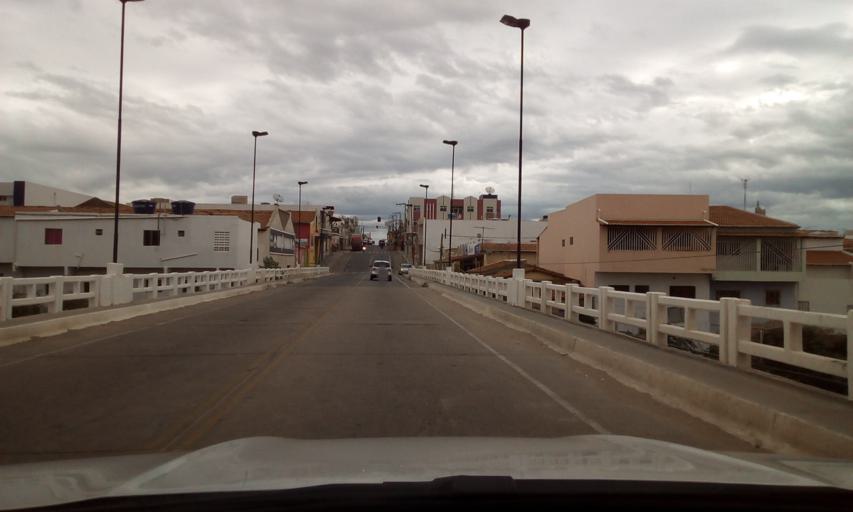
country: BR
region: Paraiba
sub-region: Picui
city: Picui
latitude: -6.5094
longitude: -36.3443
